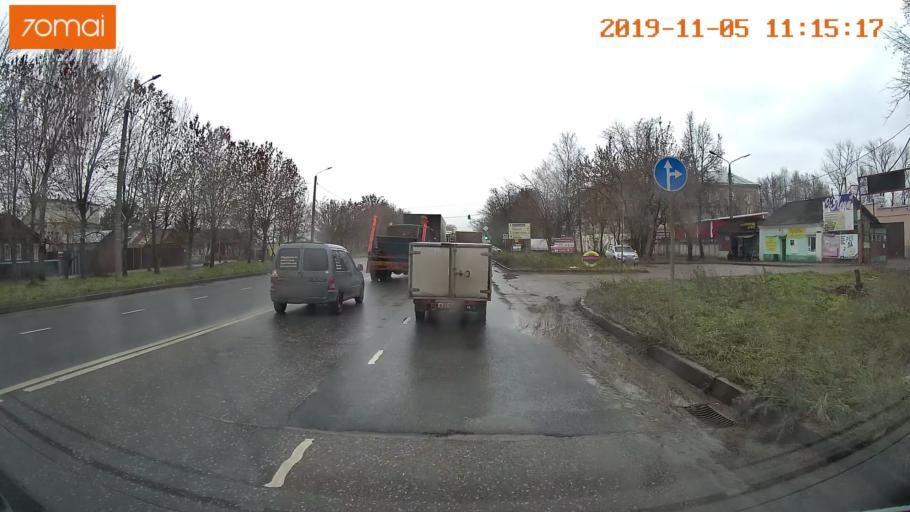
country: RU
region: Ivanovo
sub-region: Gorod Ivanovo
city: Ivanovo
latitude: 56.9772
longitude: 40.9542
